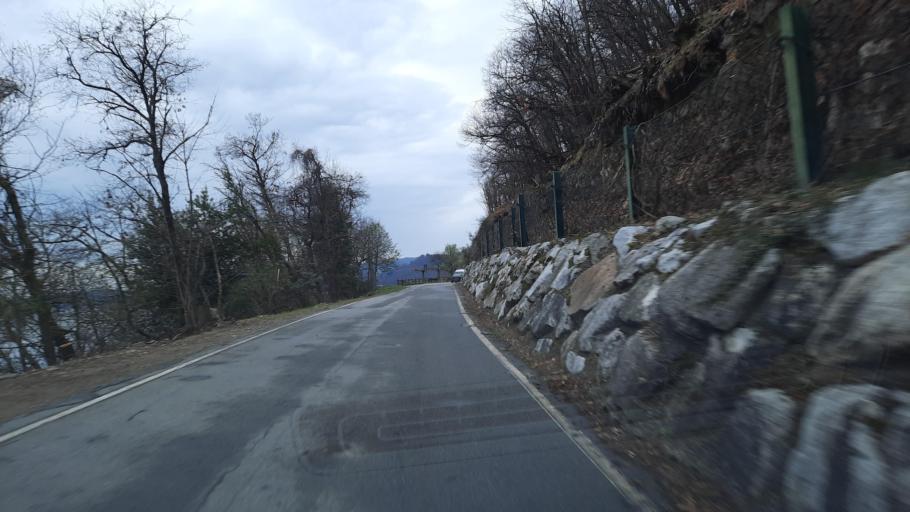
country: IT
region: Piedmont
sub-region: Provincia di Novara
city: Pella
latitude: 45.8122
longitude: 8.3864
